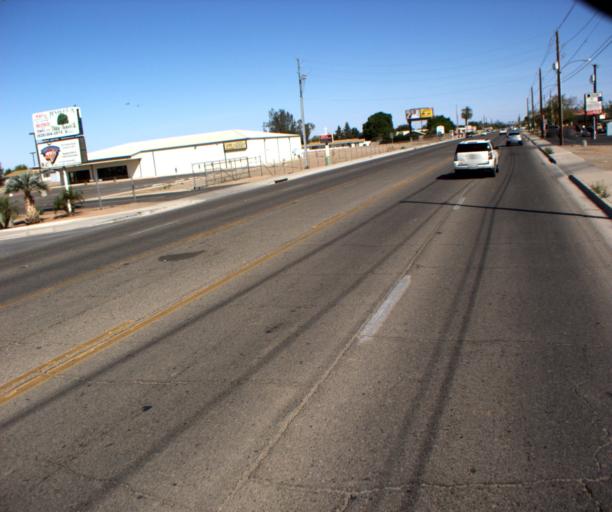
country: US
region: Arizona
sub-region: Yuma County
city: Yuma
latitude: 32.6721
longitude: -114.6501
